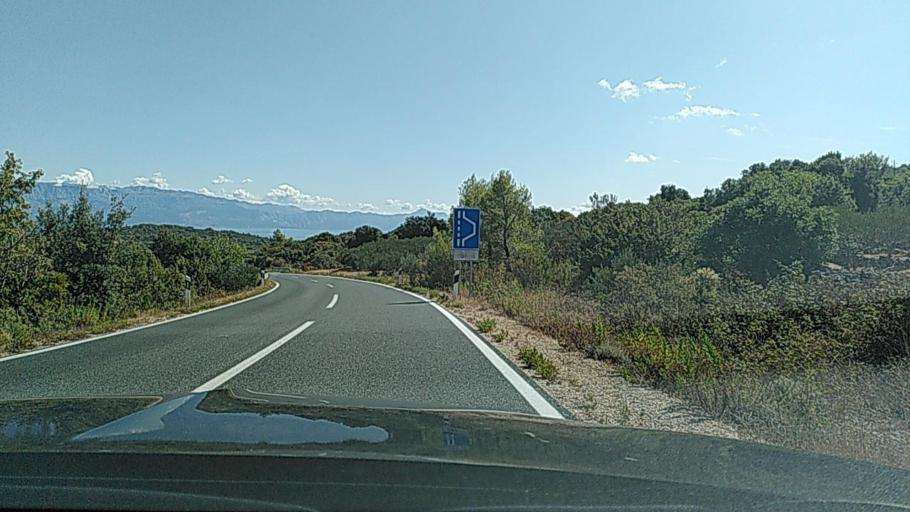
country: HR
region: Splitsko-Dalmatinska
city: Jelsa
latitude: 43.1468
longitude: 16.7826
